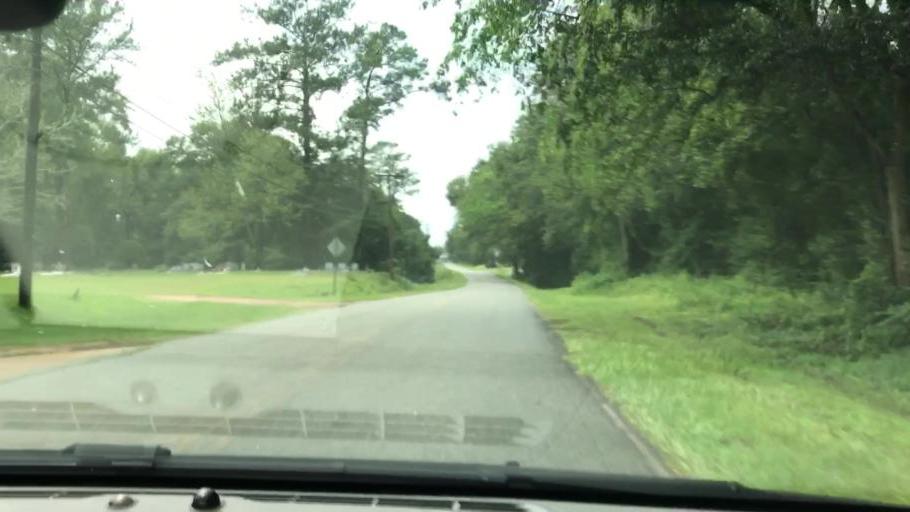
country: US
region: Georgia
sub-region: Early County
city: Blakely
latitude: 31.3747
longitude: -84.9495
